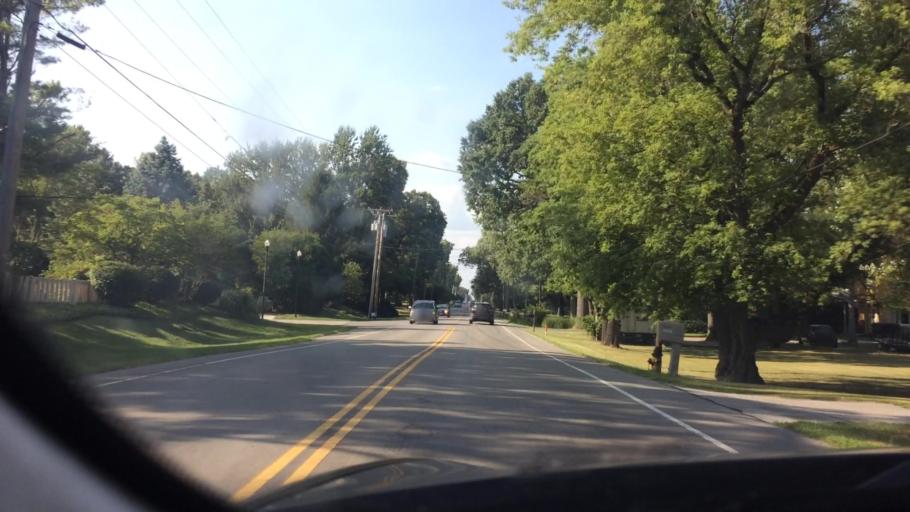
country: US
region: Ohio
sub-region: Lucas County
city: Holland
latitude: 41.6638
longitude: -83.7223
